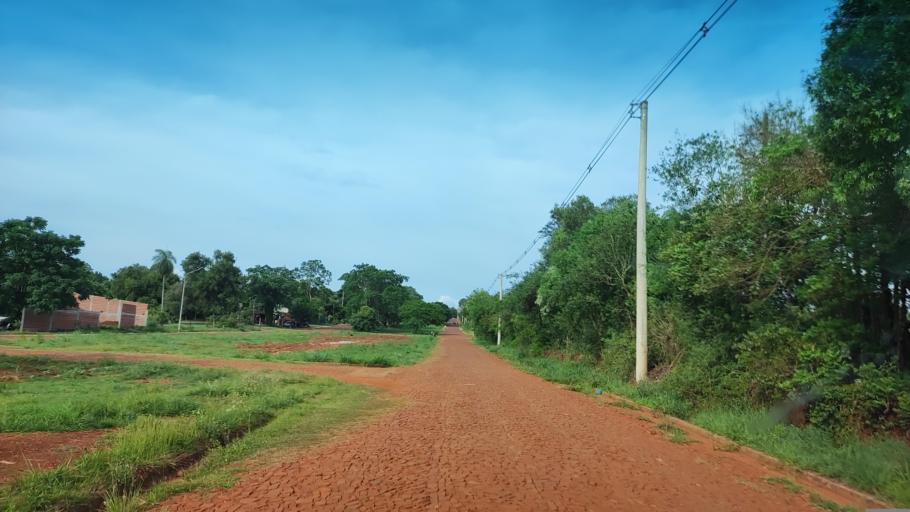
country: AR
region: Misiones
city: Gobernador Roca
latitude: -27.1353
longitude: -55.5170
